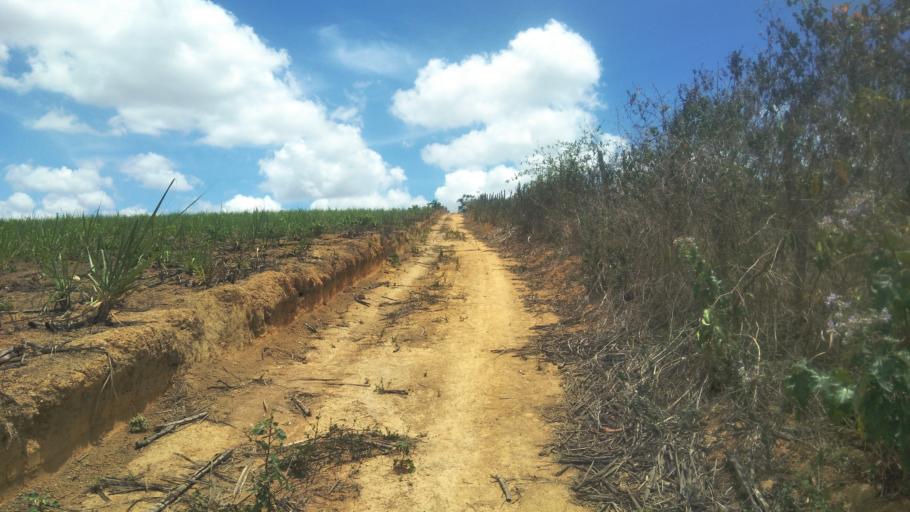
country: BR
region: Pernambuco
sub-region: Vitoria De Santo Antao
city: Vitoria de Santo Antao
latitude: -8.1517
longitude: -35.2538
